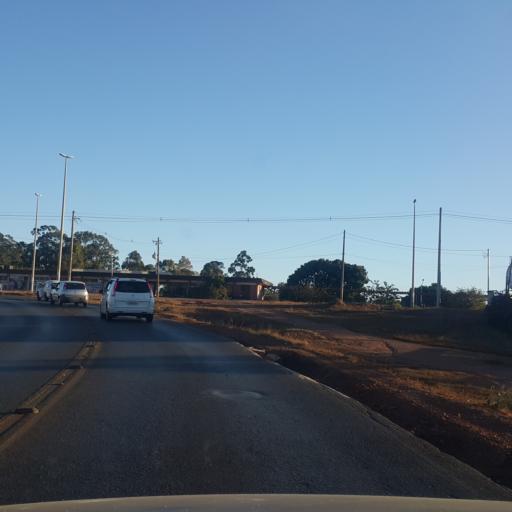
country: BR
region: Federal District
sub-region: Brasilia
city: Brasilia
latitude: -15.8599
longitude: -47.9808
